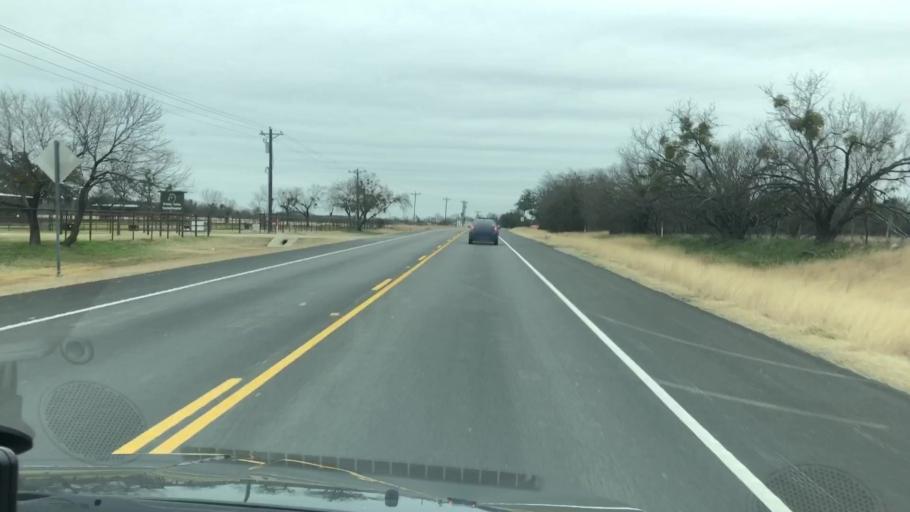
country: US
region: Texas
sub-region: Erath County
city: Stephenville
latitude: 32.3793
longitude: -98.1720
